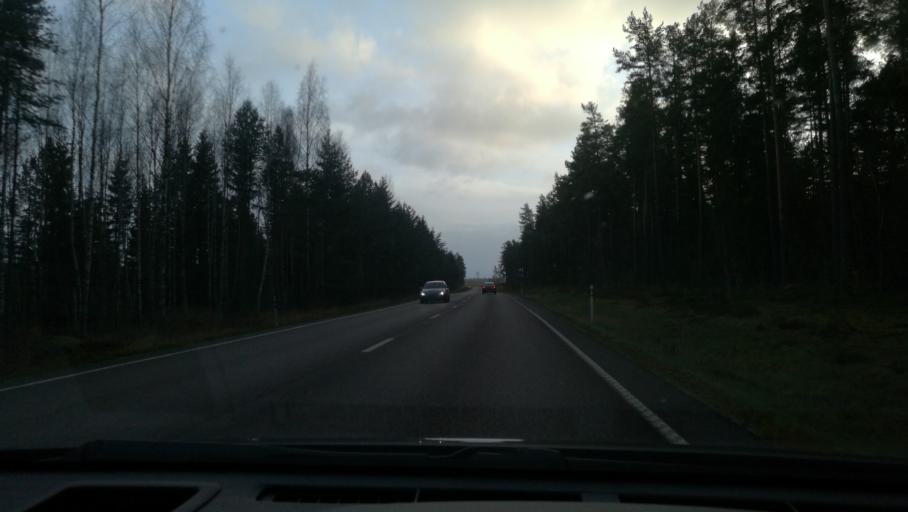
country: SE
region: Vaestmanland
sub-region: Kungsors Kommun
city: Kungsoer
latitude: 59.2068
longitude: 16.1020
